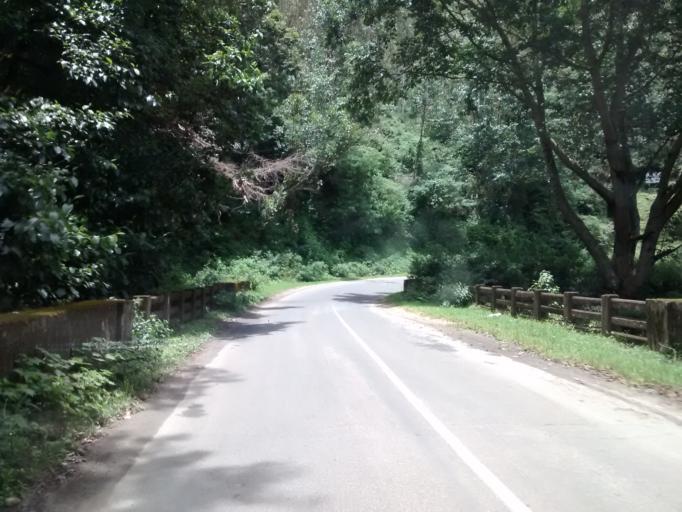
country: IN
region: Kerala
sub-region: Idukki
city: Munnar
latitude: 10.1414
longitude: 77.2053
